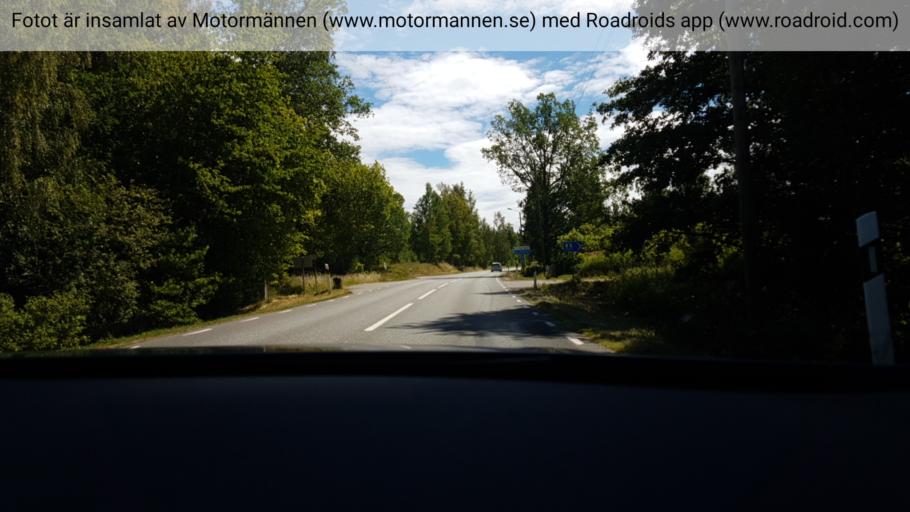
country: SE
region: Joenkoeping
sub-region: Jonkopings Kommun
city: Asa
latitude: 57.9980
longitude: 14.7424
